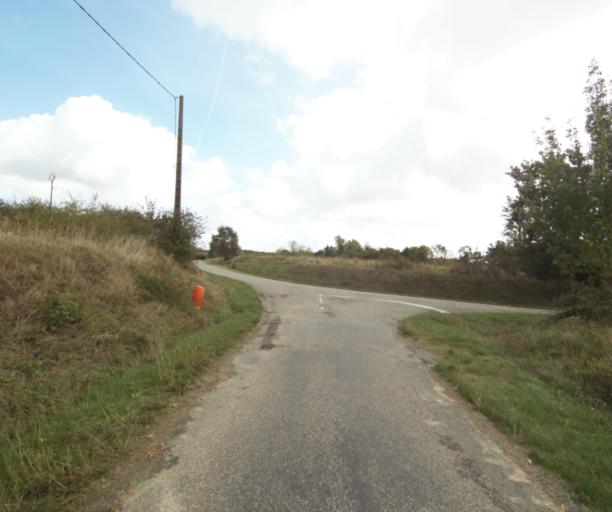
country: FR
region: Midi-Pyrenees
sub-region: Departement du Tarn-et-Garonne
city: Finhan
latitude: 43.8947
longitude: 1.1277
